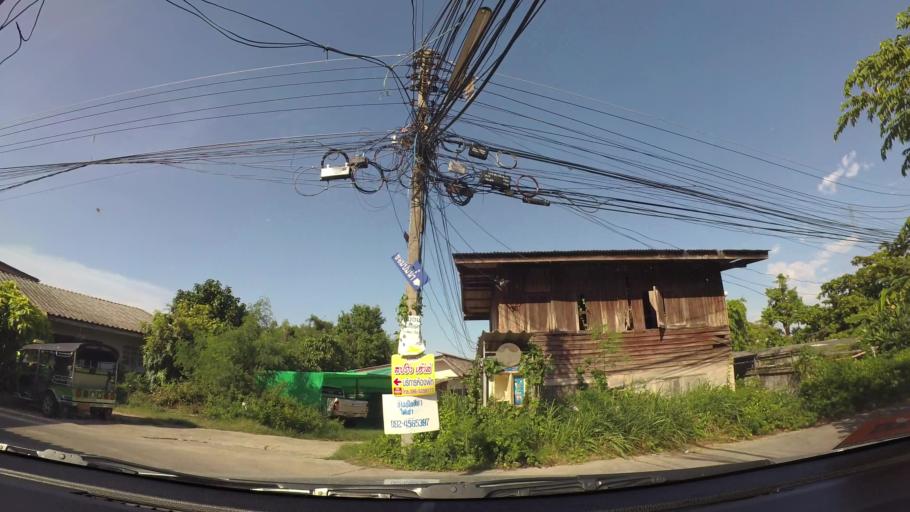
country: TH
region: Chon Buri
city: Si Racha
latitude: 13.1539
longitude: 100.9345
